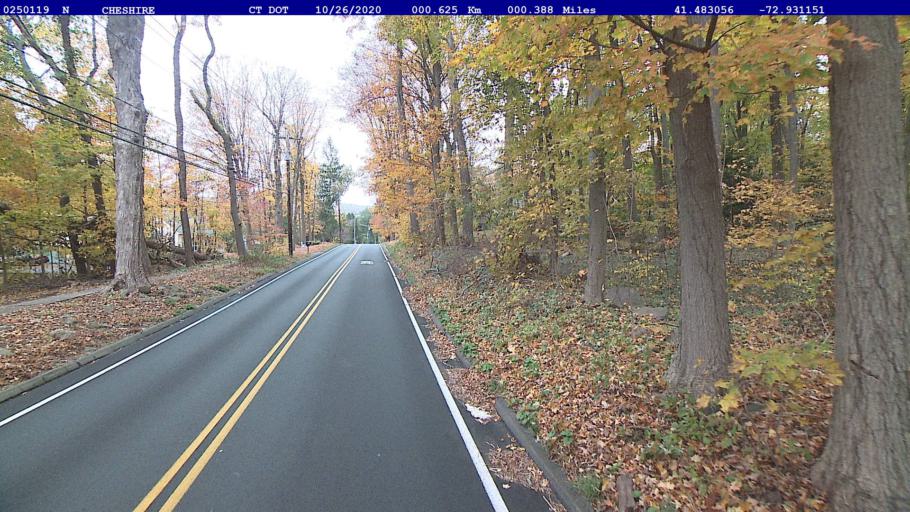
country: US
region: Connecticut
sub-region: New Haven County
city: Cheshire
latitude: 41.4831
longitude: -72.9312
